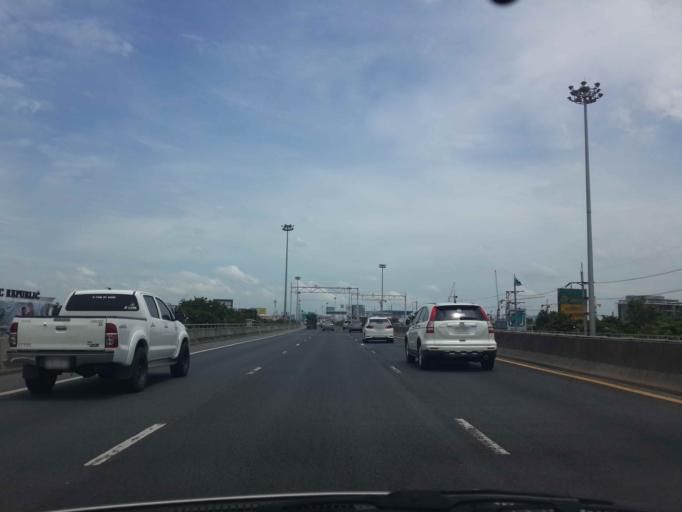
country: TH
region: Bangkok
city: Lat Phrao
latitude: 13.8098
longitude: 100.6194
